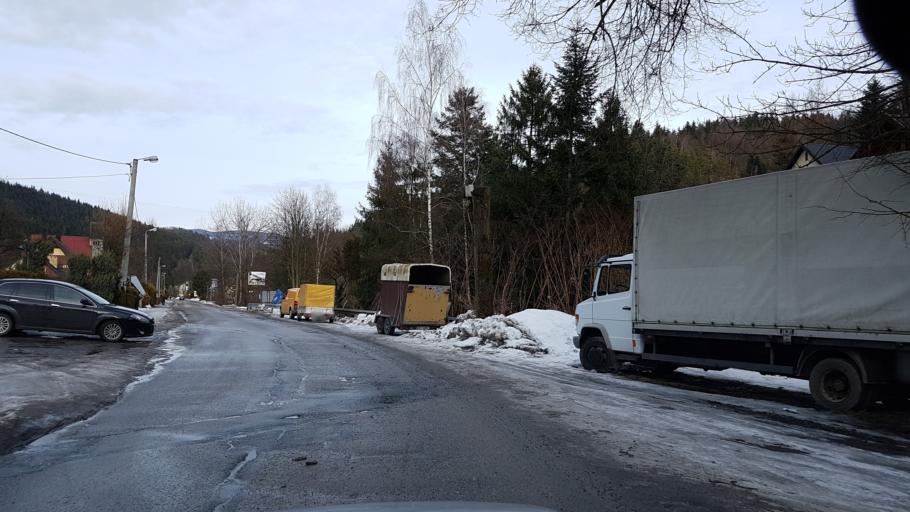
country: PL
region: Lesser Poland Voivodeship
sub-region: Powiat nowosadecki
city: Piwniczna-Zdroj
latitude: 49.4248
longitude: 20.6618
